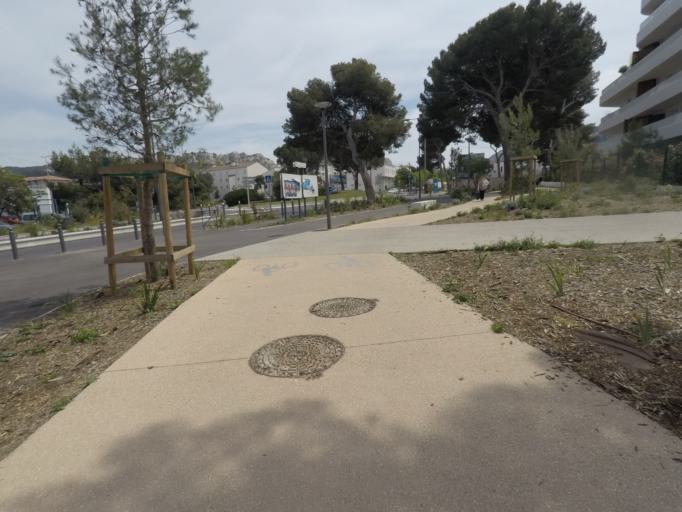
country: FR
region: Provence-Alpes-Cote d'Azur
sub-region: Departement des Bouches-du-Rhone
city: Marseille 09
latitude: 43.2324
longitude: 5.3999
